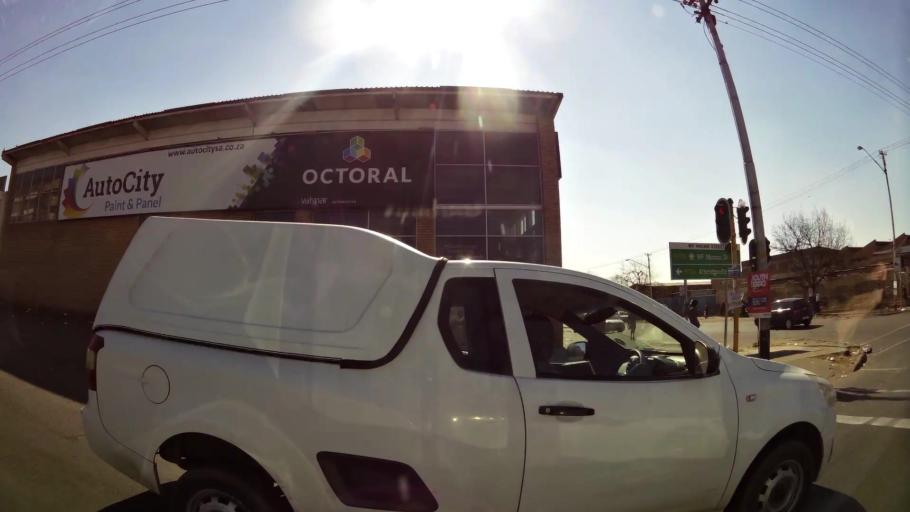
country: ZA
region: Gauteng
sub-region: City of Tshwane Metropolitan Municipality
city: Pretoria
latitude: -25.7487
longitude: 28.1547
